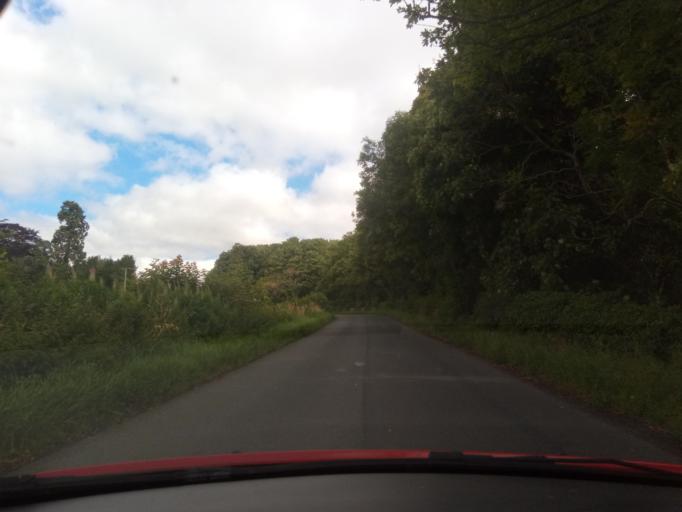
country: GB
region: Scotland
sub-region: The Scottish Borders
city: Kelso
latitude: 55.5288
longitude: -2.3573
